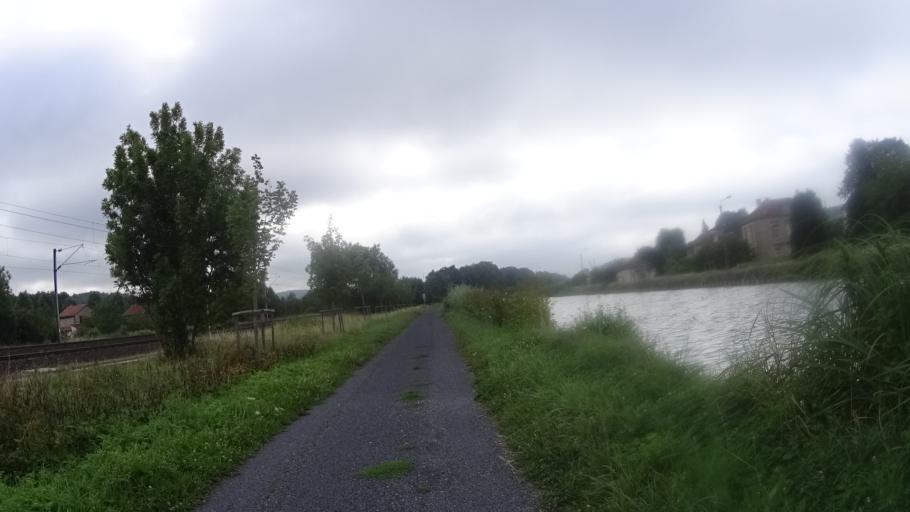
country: FR
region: Lorraine
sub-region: Departement de la Meuse
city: Fains-Veel
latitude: 48.7924
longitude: 5.1285
